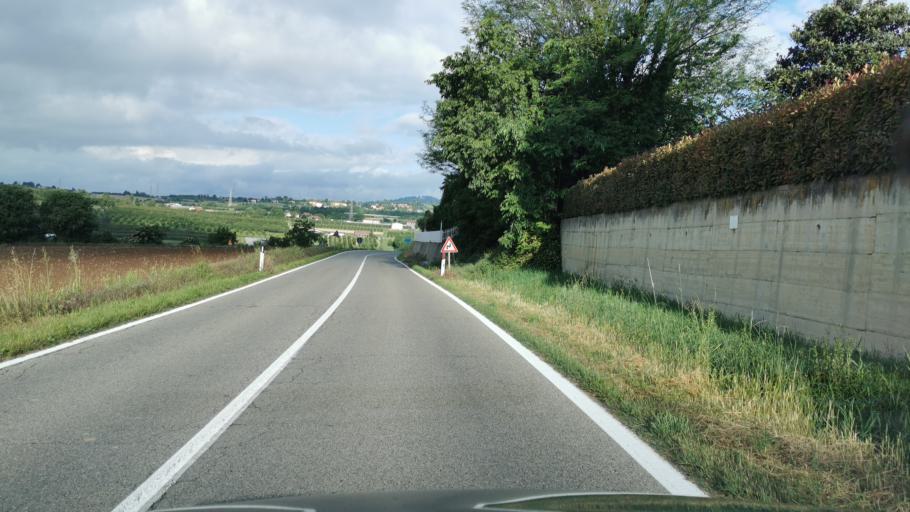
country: IT
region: Piedmont
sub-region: Provincia di Torino
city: Pino Torinese
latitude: 45.0139
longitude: 7.7805
